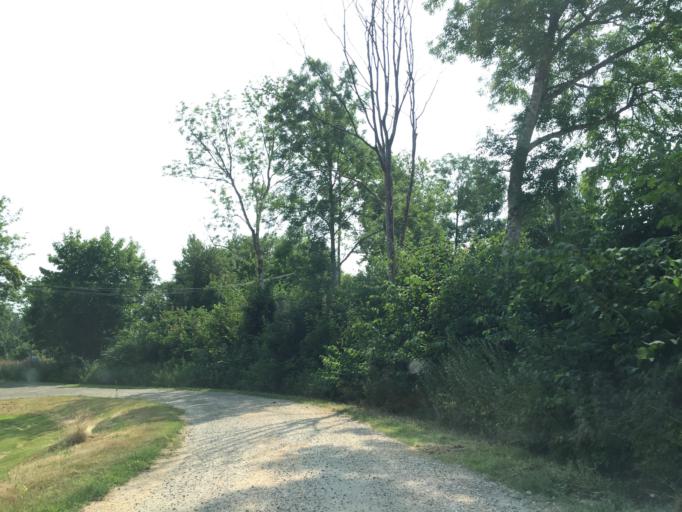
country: SE
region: Vaestra Goetaland
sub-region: Lilla Edets Kommun
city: Lilla Edet
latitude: 58.1804
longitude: 12.1110
